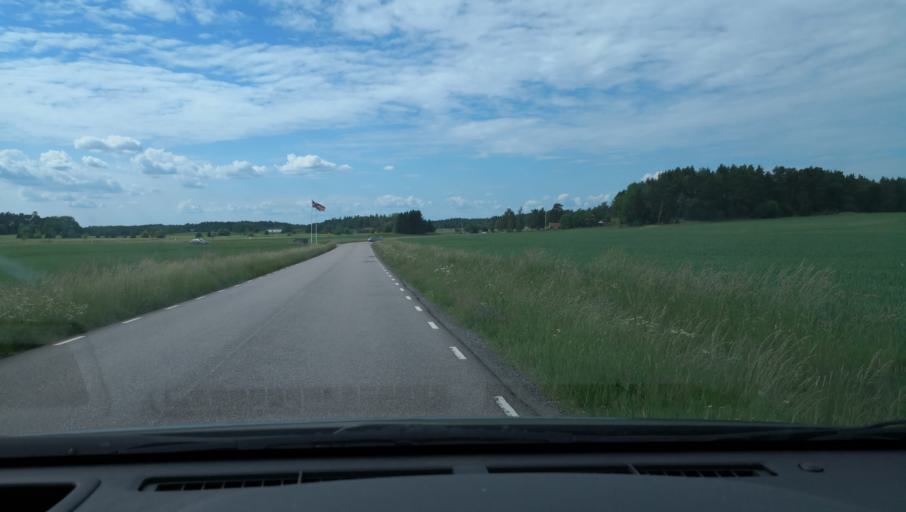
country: SE
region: Uppsala
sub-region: Uppsala Kommun
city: Uppsala
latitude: 59.8135
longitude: 17.5050
